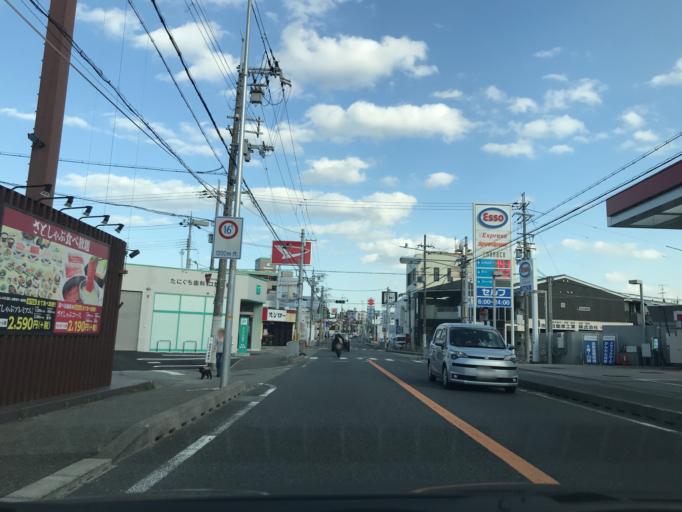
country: JP
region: Osaka
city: Ikeda
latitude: 34.8171
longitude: 135.4347
